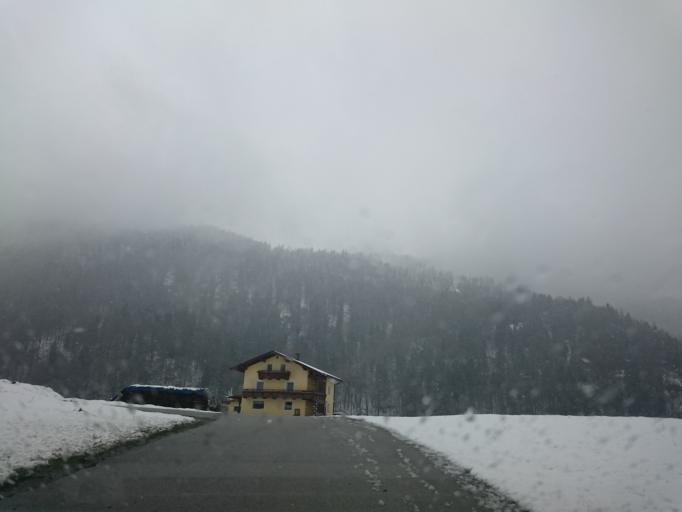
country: AT
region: Tyrol
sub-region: Politischer Bezirk Kufstein
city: Kufstein
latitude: 47.5845
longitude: 12.1527
